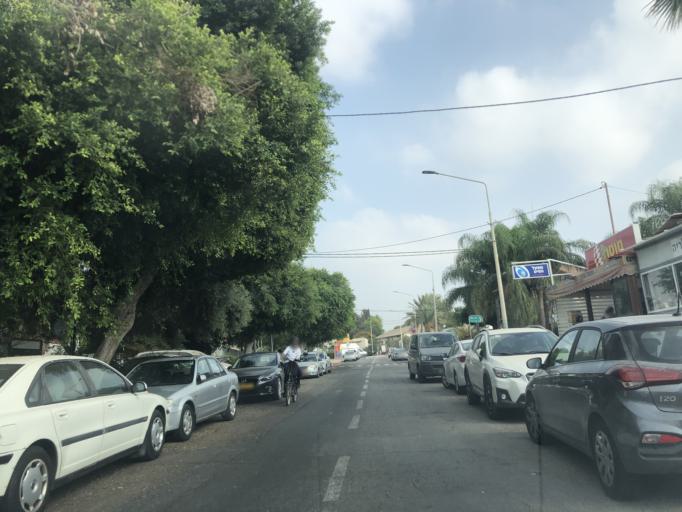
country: IL
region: Central District
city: Rosh Ha'Ayin
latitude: 32.0964
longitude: 34.9490
